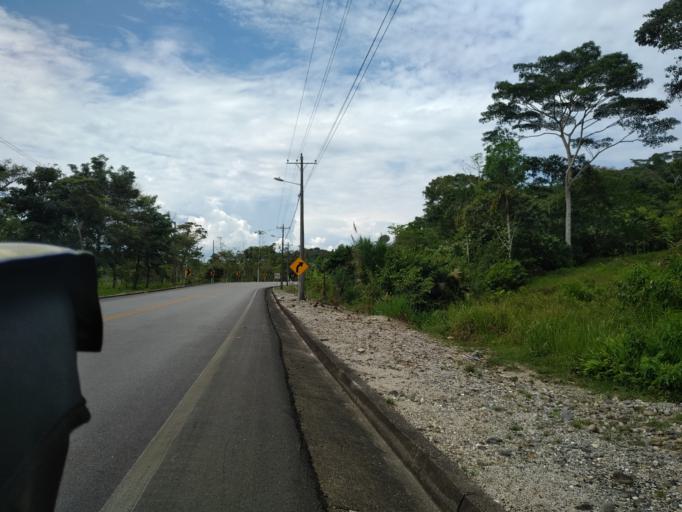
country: EC
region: Napo
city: Tena
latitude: -1.1493
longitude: -77.8449
